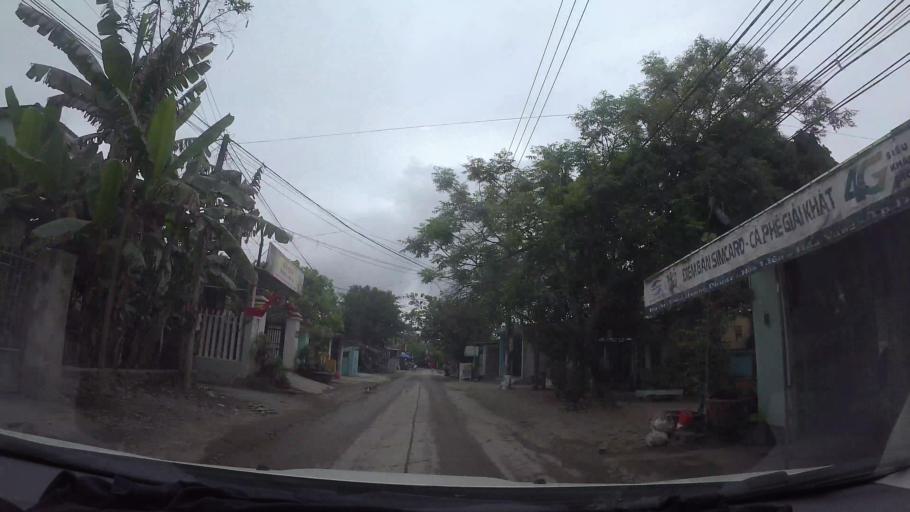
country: VN
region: Da Nang
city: Lien Chieu
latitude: 16.0779
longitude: 108.0987
